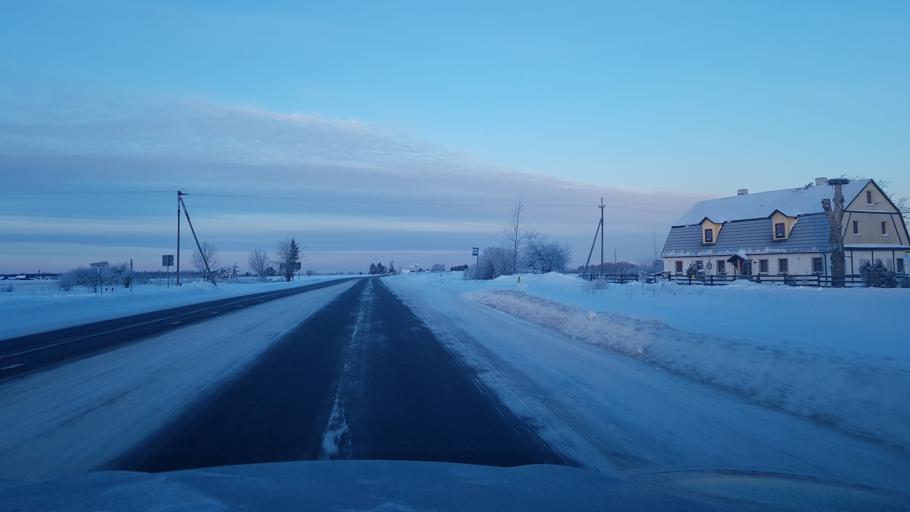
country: EE
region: Ida-Virumaa
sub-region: Narva-Joesuu linn
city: Narva-Joesuu
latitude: 59.4013
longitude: 28.0630
